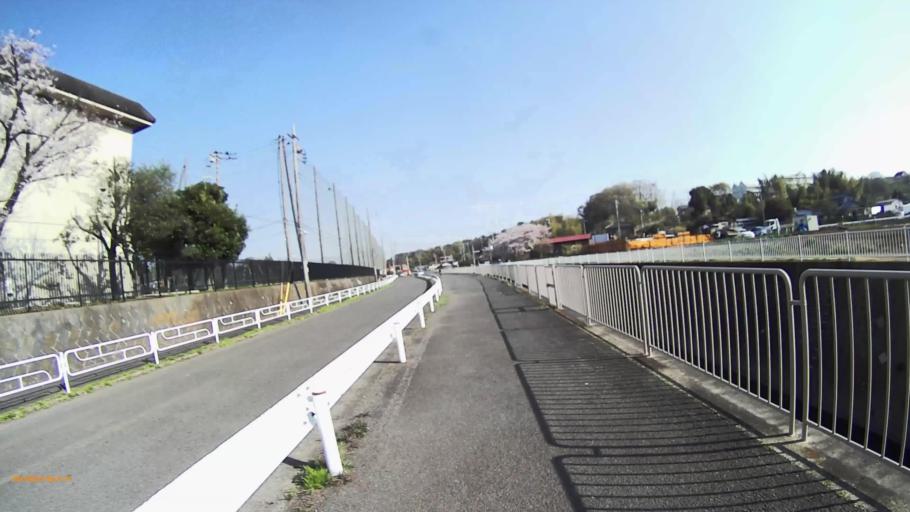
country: JP
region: Kanagawa
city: Atsugi
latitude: 35.4367
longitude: 139.4133
